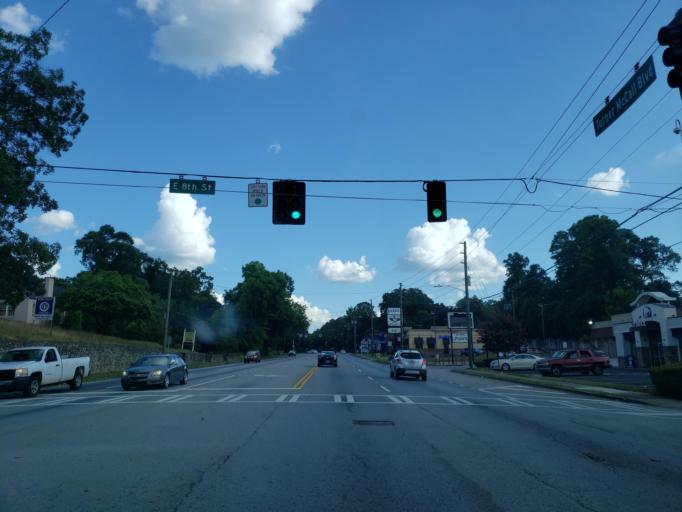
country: US
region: Georgia
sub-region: Floyd County
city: Rome
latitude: 34.2433
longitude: -85.1613
